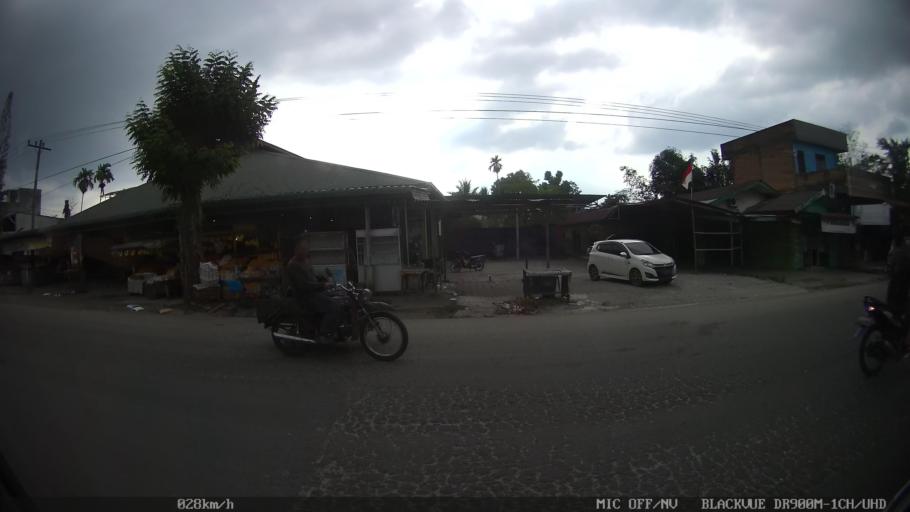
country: ID
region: North Sumatra
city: Sunggal
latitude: 3.5272
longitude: 98.6197
